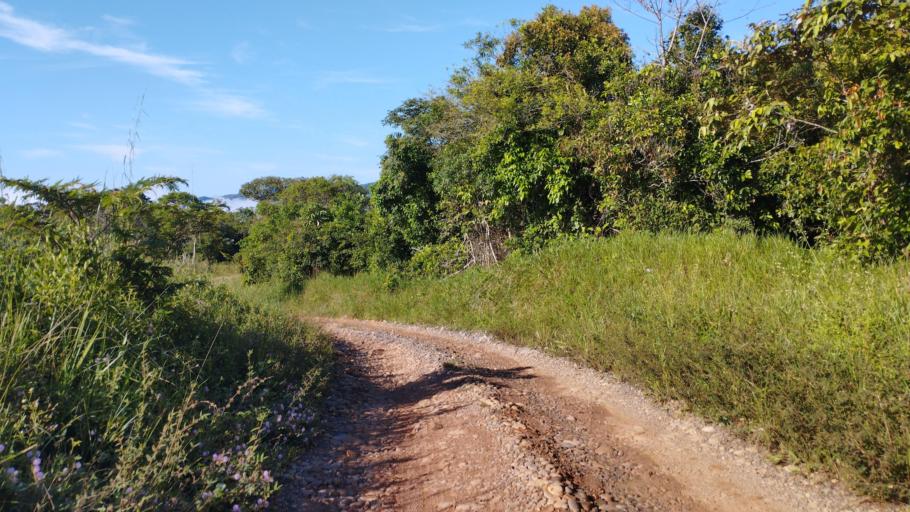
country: CO
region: Casanare
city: Sabanalarga
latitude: 4.7750
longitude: -73.0812
